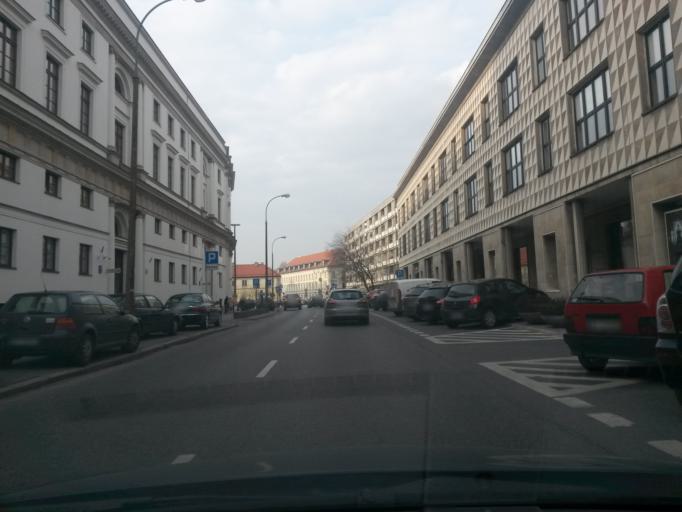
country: PL
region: Masovian Voivodeship
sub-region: Warszawa
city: Warsaw
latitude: 52.2437
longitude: 21.0118
